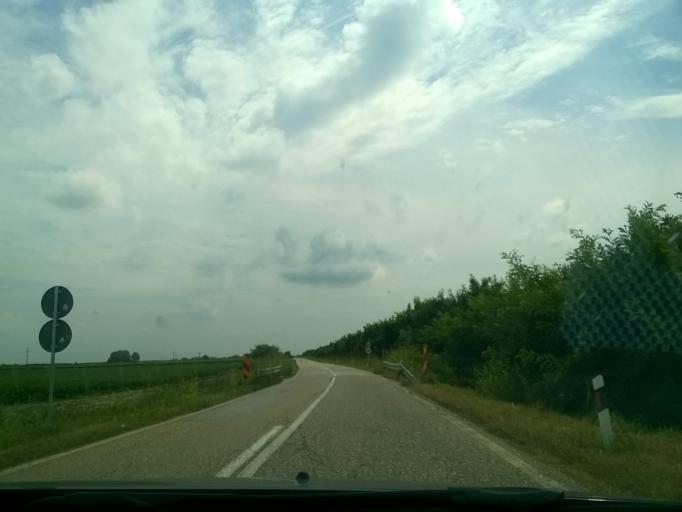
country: RS
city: Hajducica
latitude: 45.2420
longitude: 20.9833
